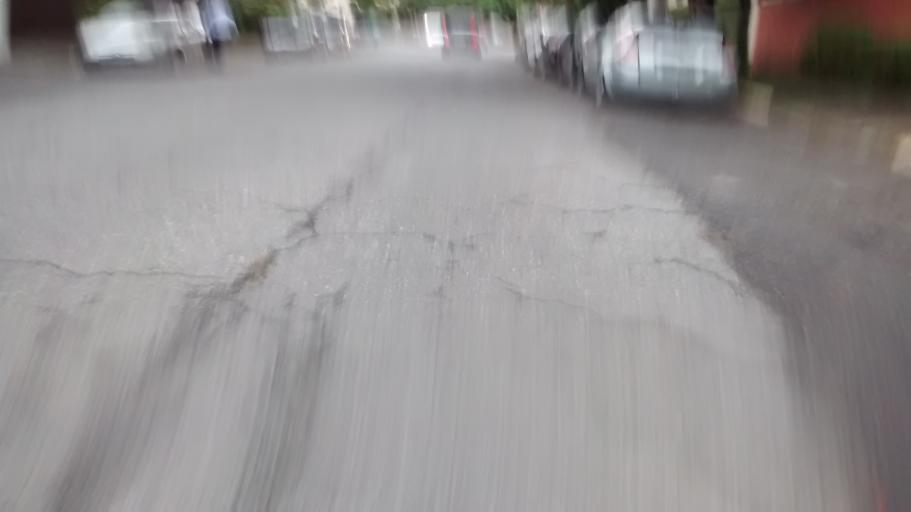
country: BR
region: Sao Paulo
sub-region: Sao Paulo
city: Sao Paulo
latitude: -23.5747
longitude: -46.6912
